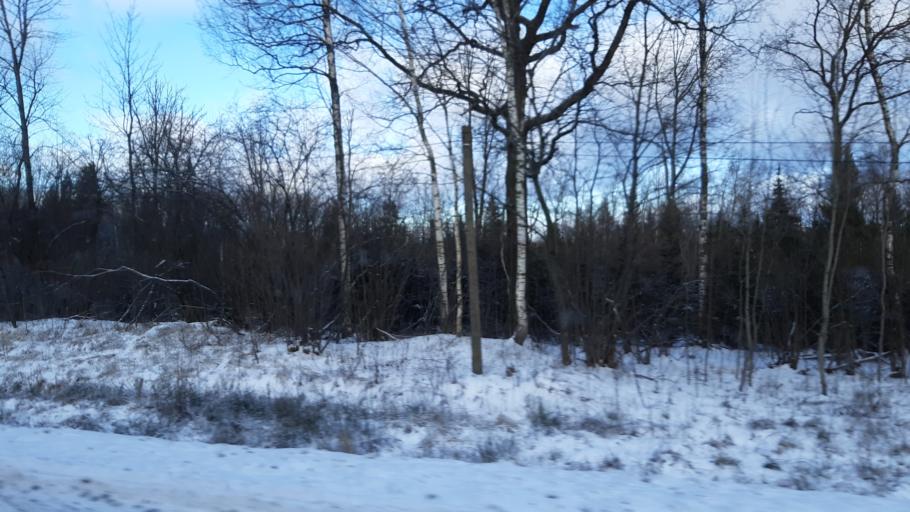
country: RU
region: Moskovskaya
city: Svatkovo
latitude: 56.3154
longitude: 38.3064
